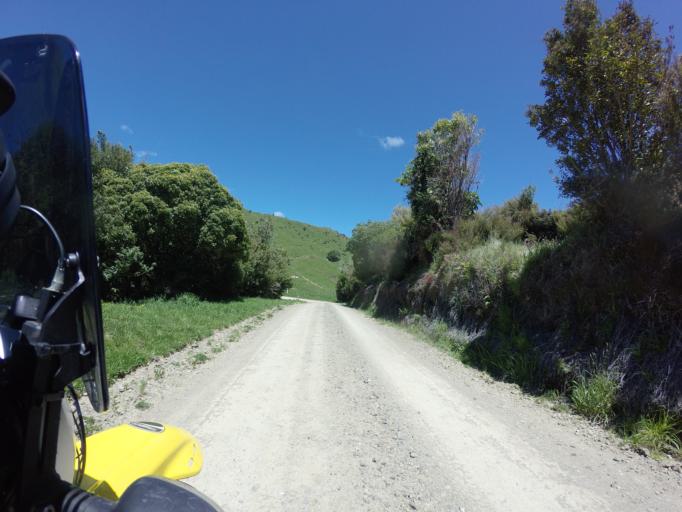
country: NZ
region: Bay of Plenty
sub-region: Opotiki District
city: Opotiki
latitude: -38.4086
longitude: 177.4446
